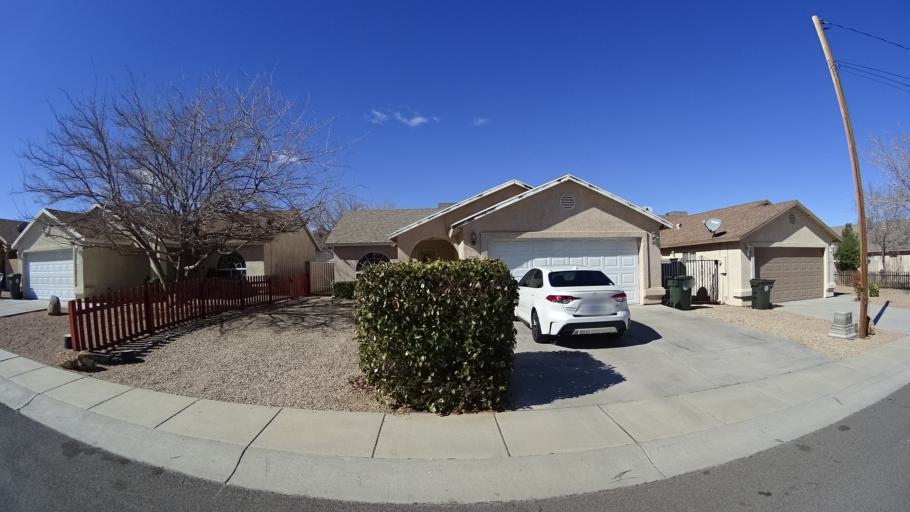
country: US
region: Arizona
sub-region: Mohave County
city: New Kingman-Butler
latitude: 35.2201
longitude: -114.0002
